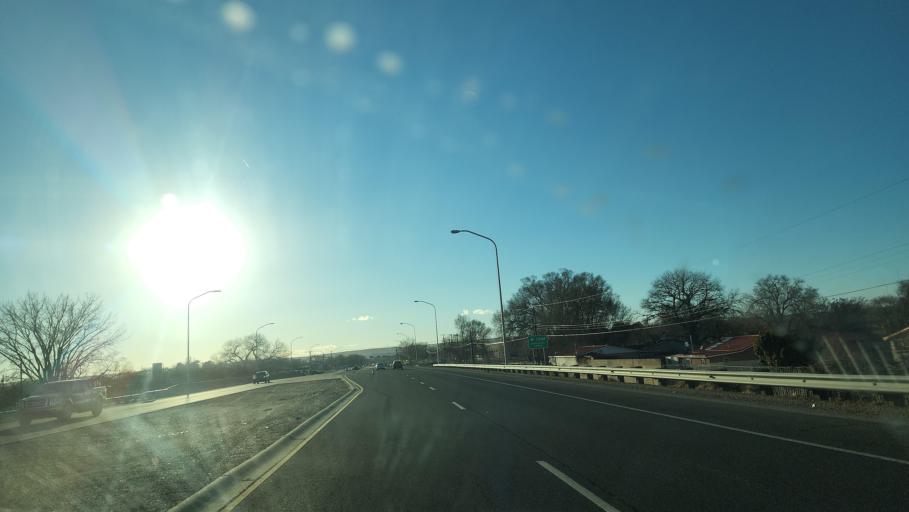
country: US
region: New Mexico
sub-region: Bernalillo County
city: South Valley
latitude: 35.0272
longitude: -106.6767
